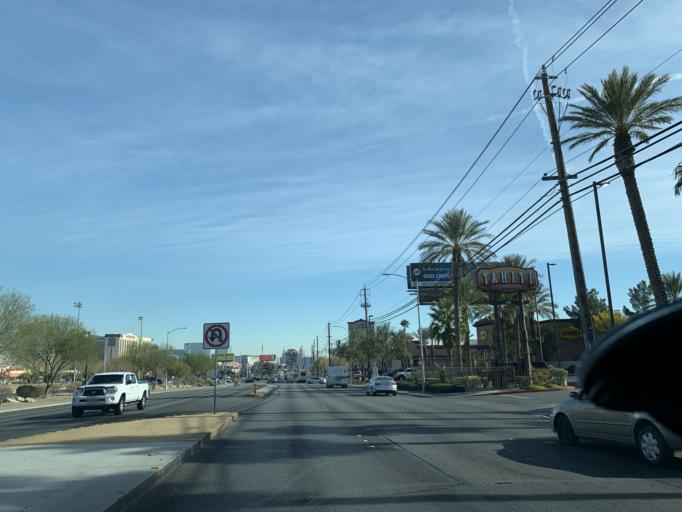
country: US
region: Nevada
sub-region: Clark County
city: Spring Valley
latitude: 36.1007
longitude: -115.2109
